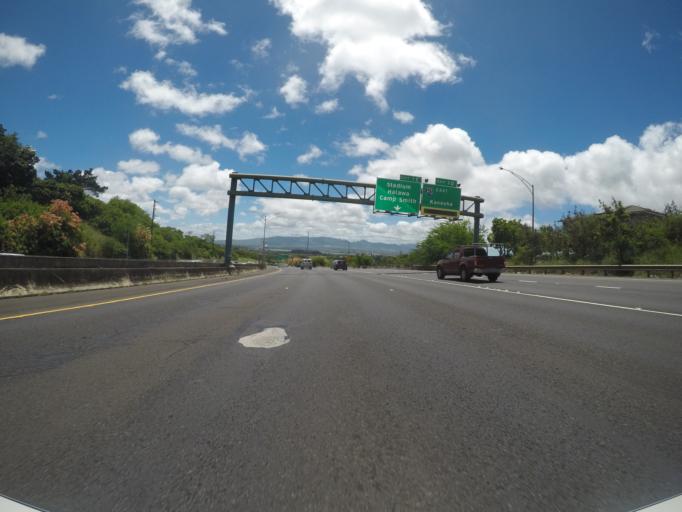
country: US
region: Hawaii
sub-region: Honolulu County
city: Halawa Heights
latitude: 21.3684
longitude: -157.9069
